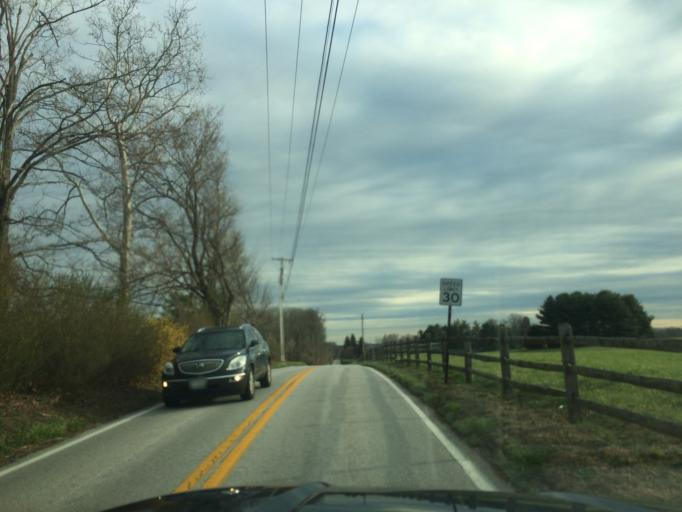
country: US
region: Maryland
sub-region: Howard County
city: North Laurel
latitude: 39.1510
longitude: -76.8606
